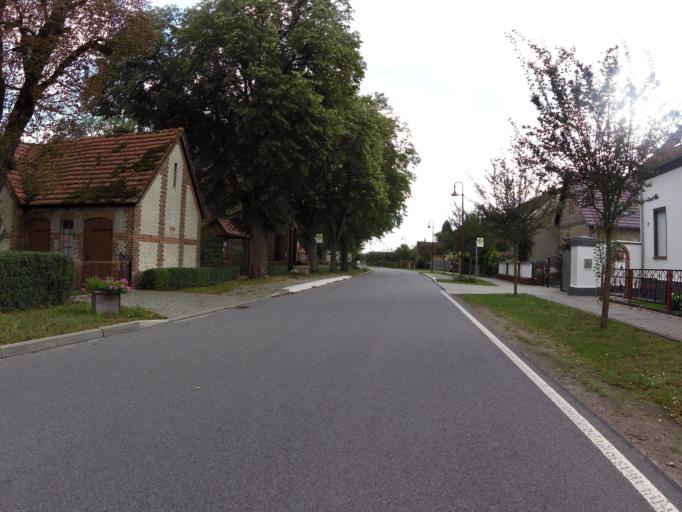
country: DE
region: Brandenburg
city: Munchehofe
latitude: 52.2142
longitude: 13.8730
